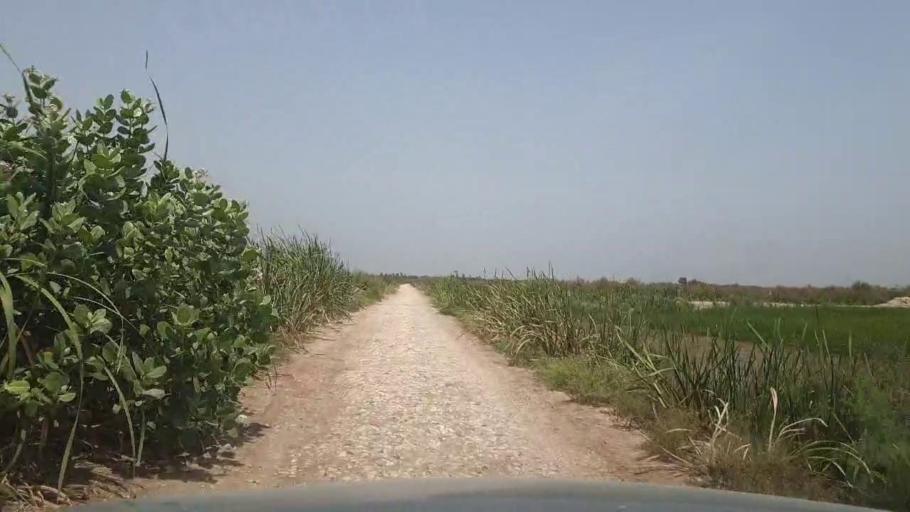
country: PK
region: Sindh
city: Garhi Yasin
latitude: 27.9478
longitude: 68.4302
